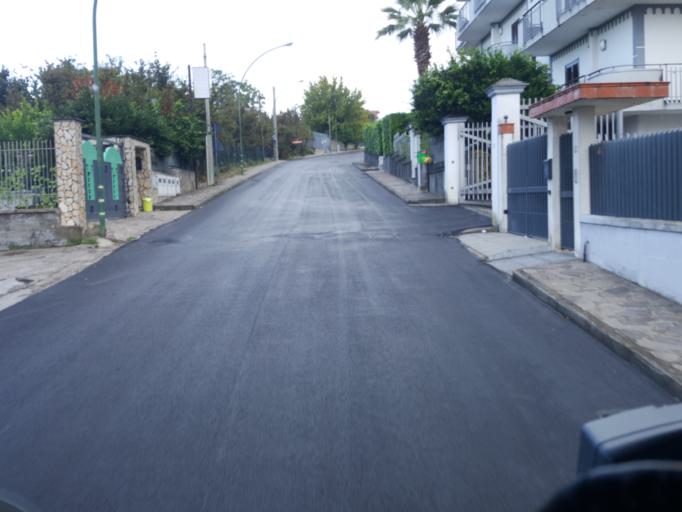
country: IT
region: Campania
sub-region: Provincia di Avellino
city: Domicella
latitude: 40.8808
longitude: 14.5865
